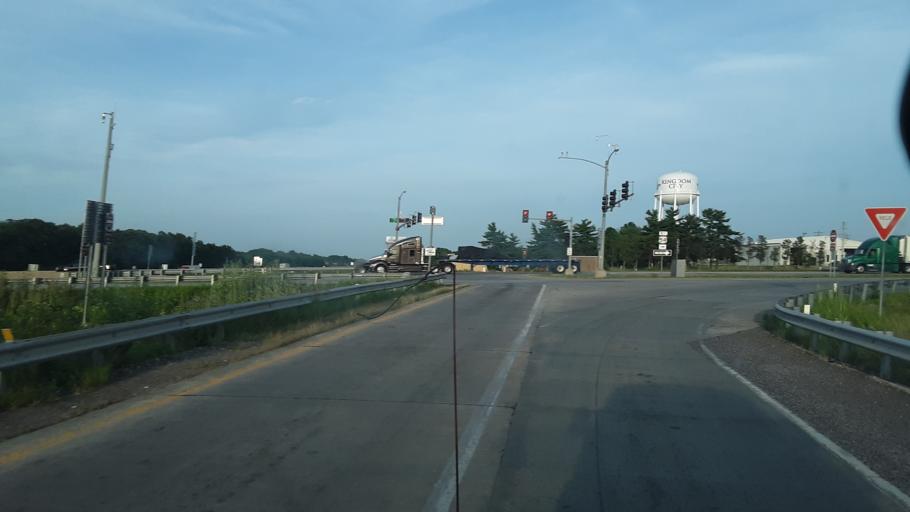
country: US
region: Missouri
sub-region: Callaway County
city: Fulton
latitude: 38.9438
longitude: -91.9418
